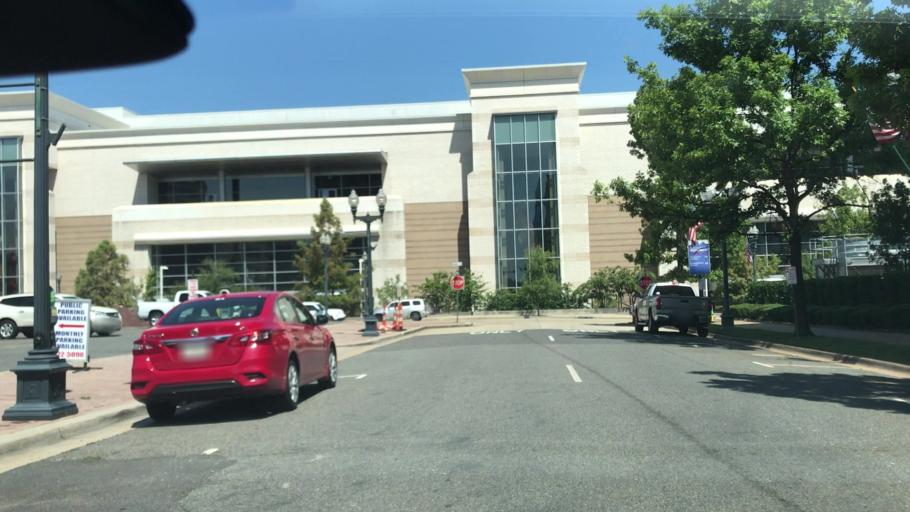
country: US
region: Louisiana
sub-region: Caddo Parish
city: Shreveport
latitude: 32.5156
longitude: -93.7508
